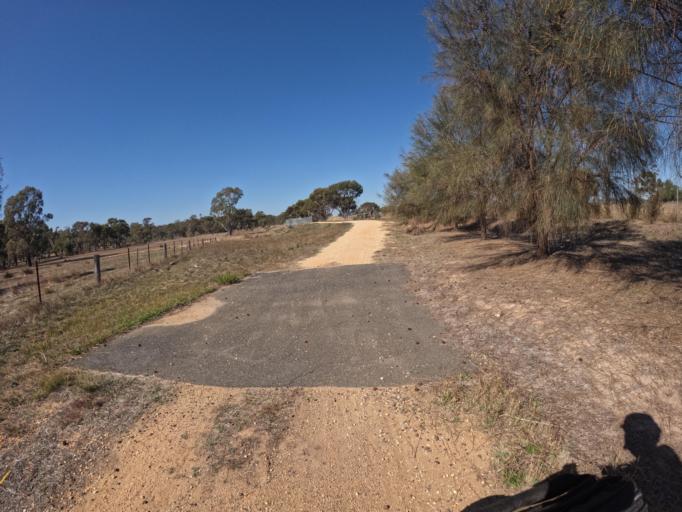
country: AU
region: Victoria
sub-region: Greater Bendigo
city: Kennington
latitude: -36.8293
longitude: 144.5893
